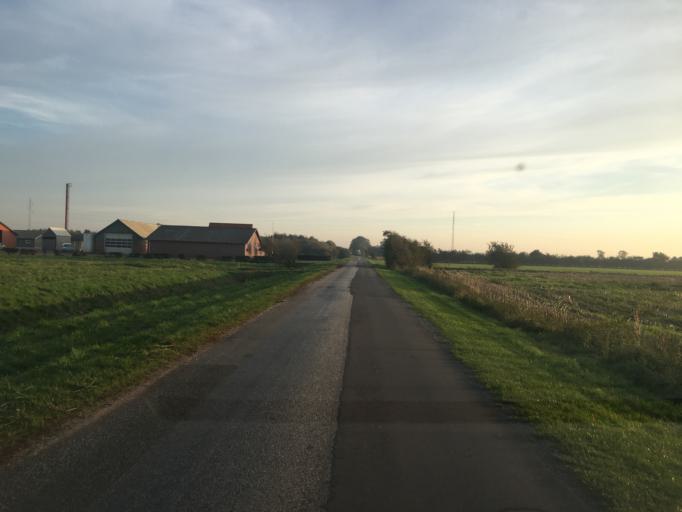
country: DK
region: South Denmark
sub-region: Tonder Kommune
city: Logumkloster
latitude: 55.0543
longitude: 9.0239
